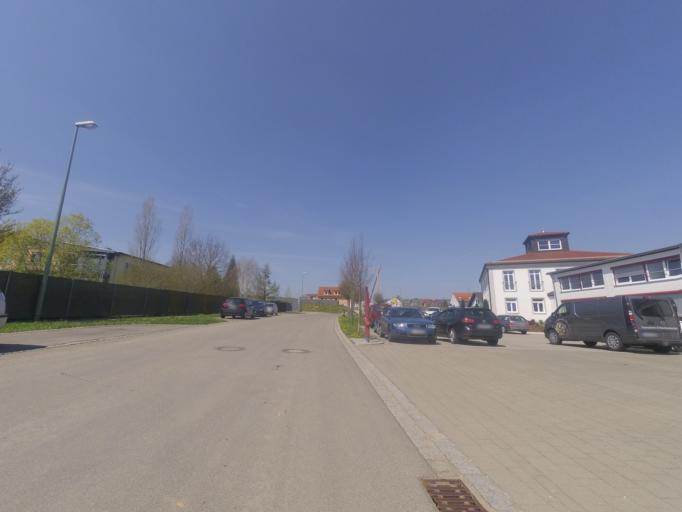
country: DE
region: Bavaria
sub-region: Swabia
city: Roggenburg
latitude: 48.2867
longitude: 10.2088
